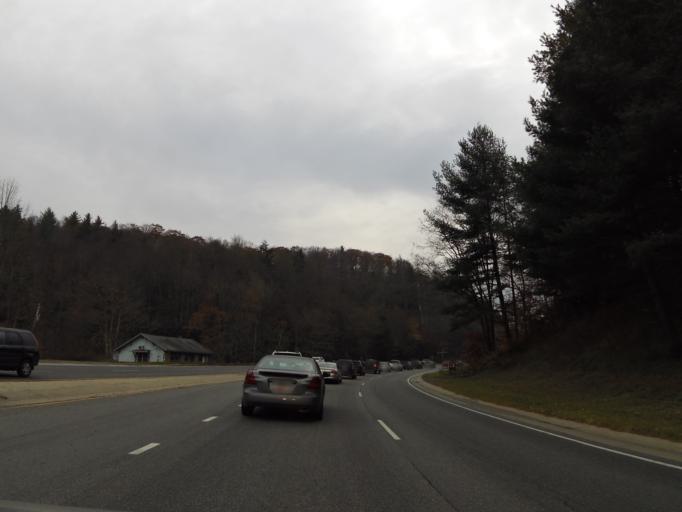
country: US
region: North Carolina
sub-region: Watauga County
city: Blowing Rock
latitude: 36.1458
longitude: -81.6639
